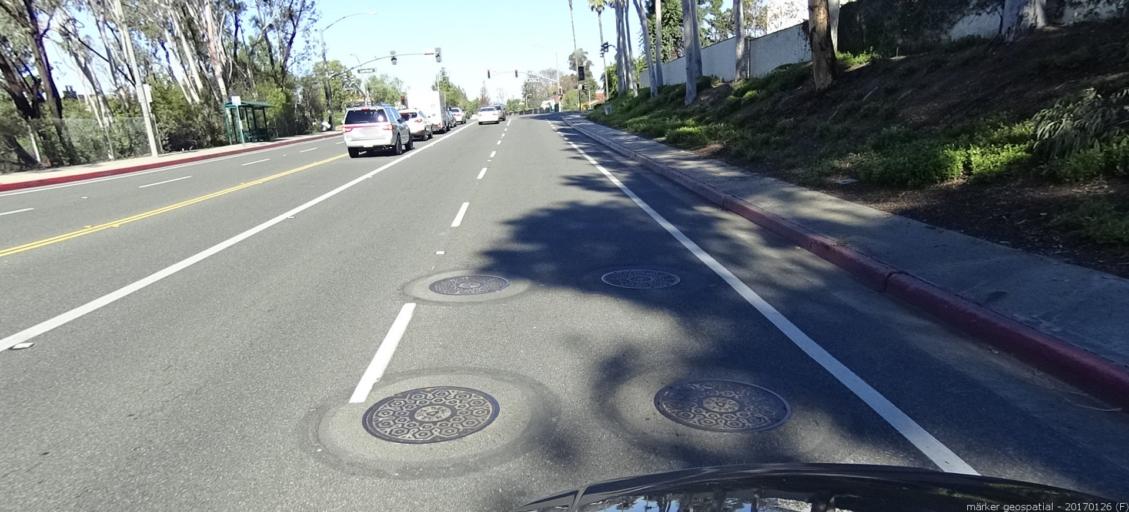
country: US
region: California
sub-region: Orange County
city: Lake Forest
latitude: 33.6397
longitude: -117.7029
